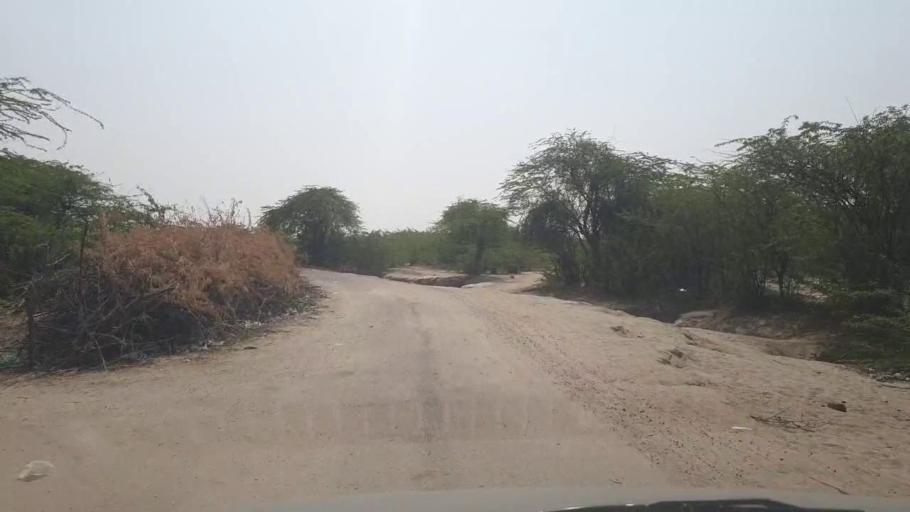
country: PK
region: Sindh
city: Chor
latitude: 25.4875
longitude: 69.7830
